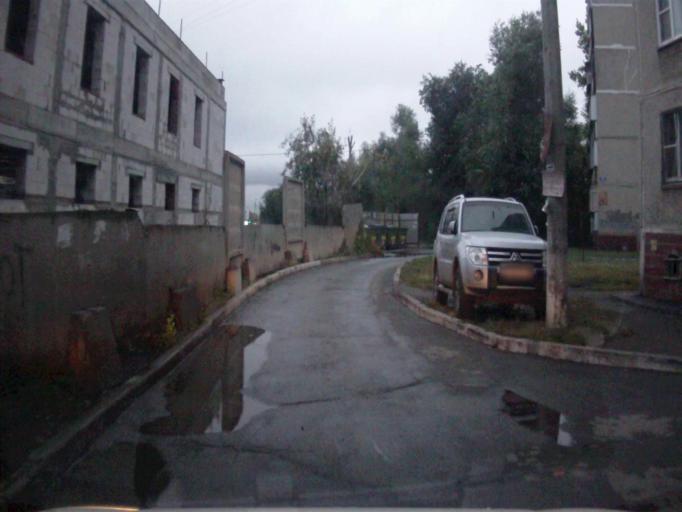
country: RU
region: Chelyabinsk
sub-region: Gorod Chelyabinsk
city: Chelyabinsk
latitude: 55.1408
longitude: 61.4532
